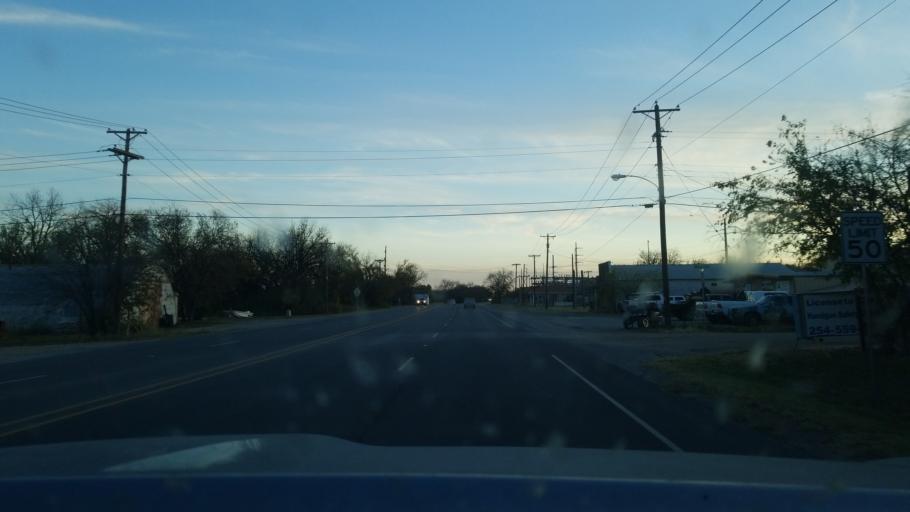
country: US
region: Texas
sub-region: Stephens County
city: Breckenridge
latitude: 32.7499
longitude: -98.9027
